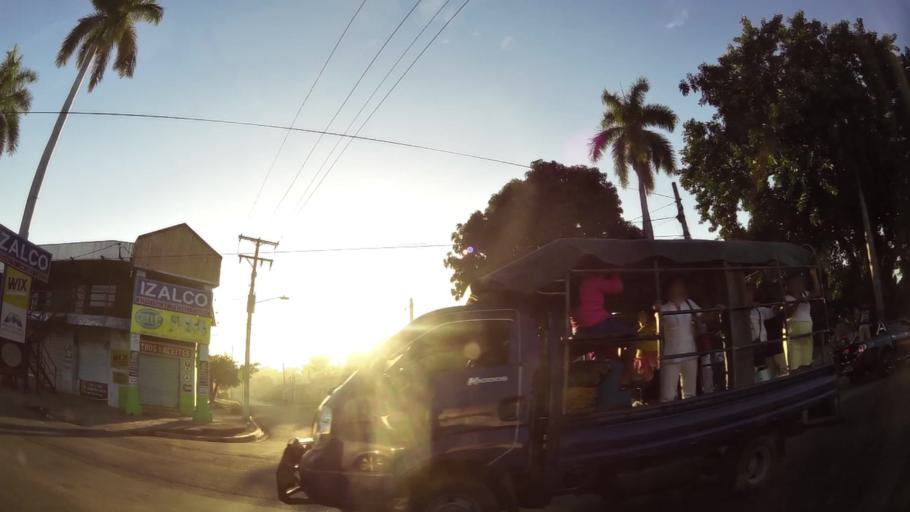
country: SV
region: Sonsonate
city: Sonsonate
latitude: 13.7240
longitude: -89.7182
